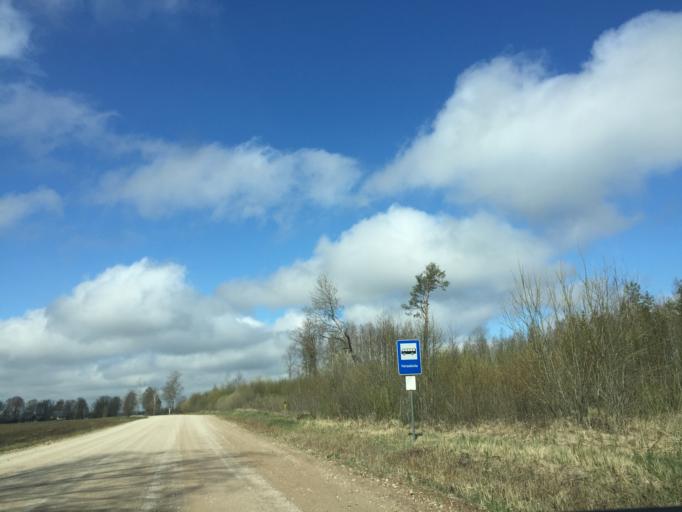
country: LV
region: Apes Novads
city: Ape
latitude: 57.4764
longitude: 26.4669
